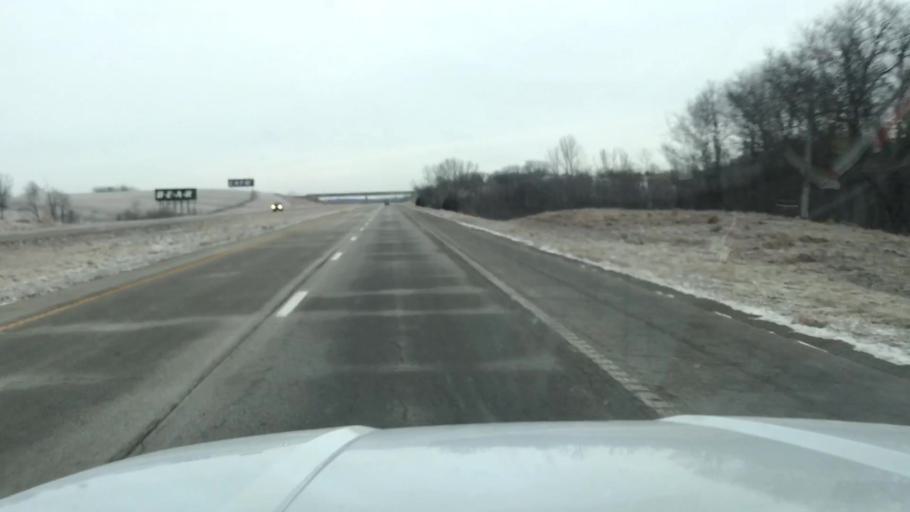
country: US
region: Missouri
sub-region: Andrew County
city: Savannah
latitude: 39.8936
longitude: -94.8570
